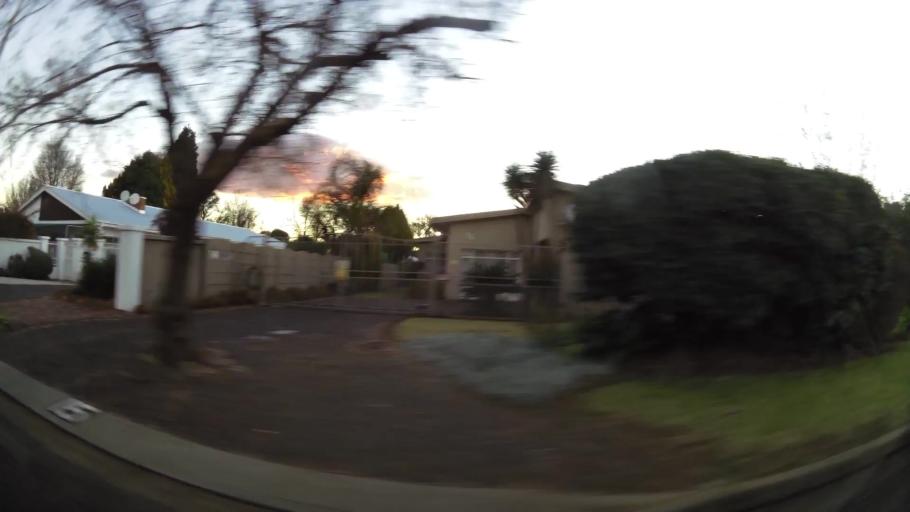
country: ZA
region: North-West
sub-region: Dr Kenneth Kaunda District Municipality
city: Potchefstroom
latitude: -26.7110
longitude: 27.1162
